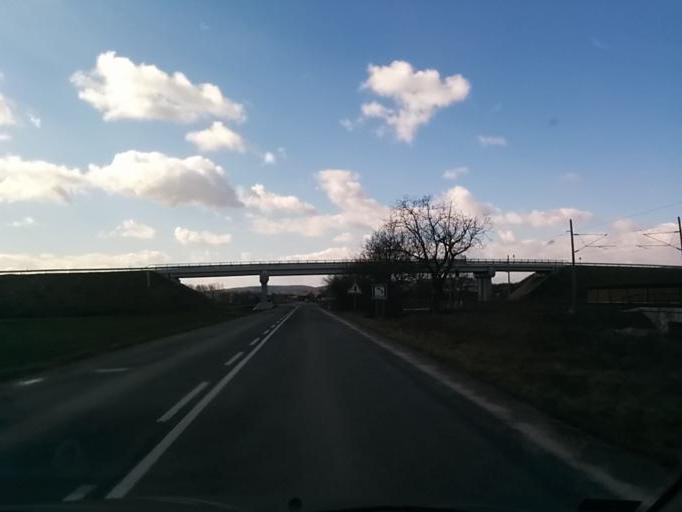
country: SK
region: Trenciansky
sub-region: Okres Nove Mesto nad Vahom
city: Nove Mesto nad Vahom
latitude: 48.8357
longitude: 17.9183
